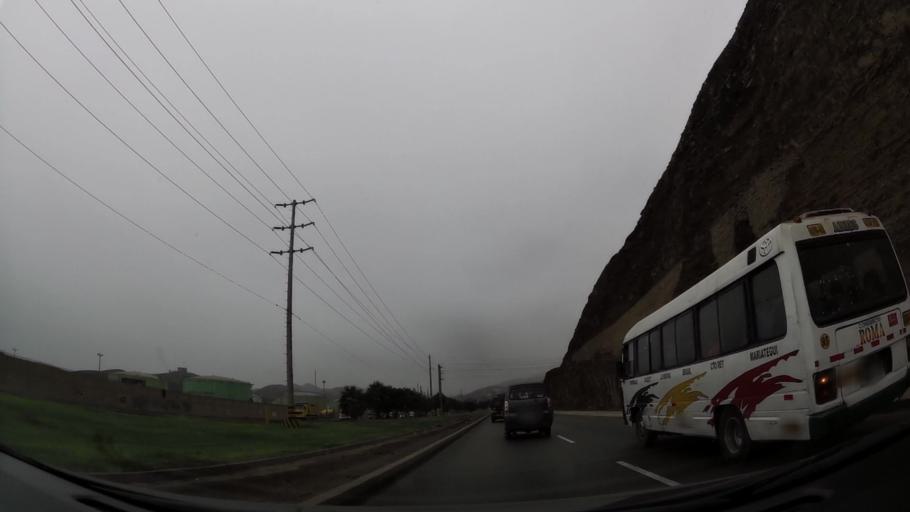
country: PE
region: Lima
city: Ventanilla
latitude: -11.9278
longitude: -77.1299
